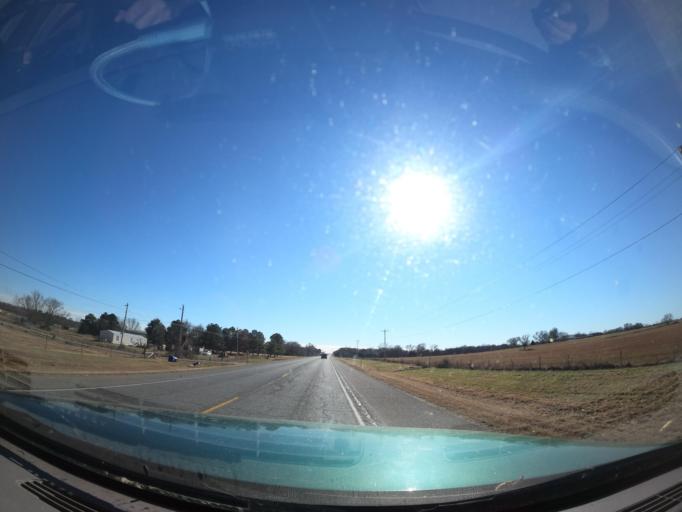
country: US
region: Oklahoma
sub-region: Muskogee County
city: Haskell
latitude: 35.8485
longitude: -95.6775
